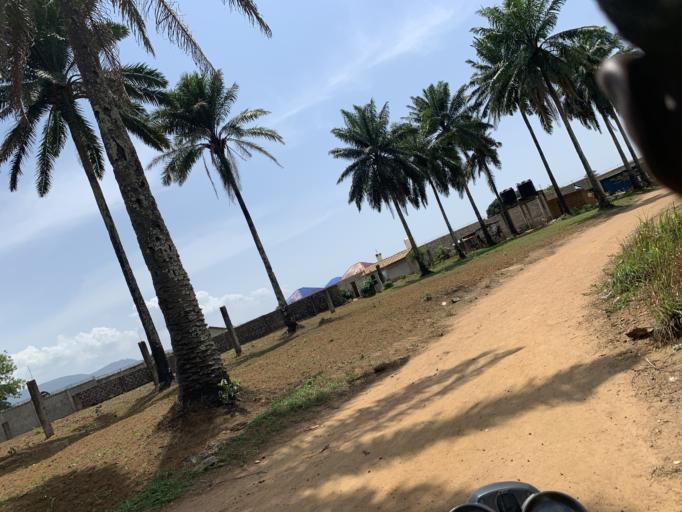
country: SL
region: Western Area
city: Waterloo
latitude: 8.3387
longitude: -13.0368
